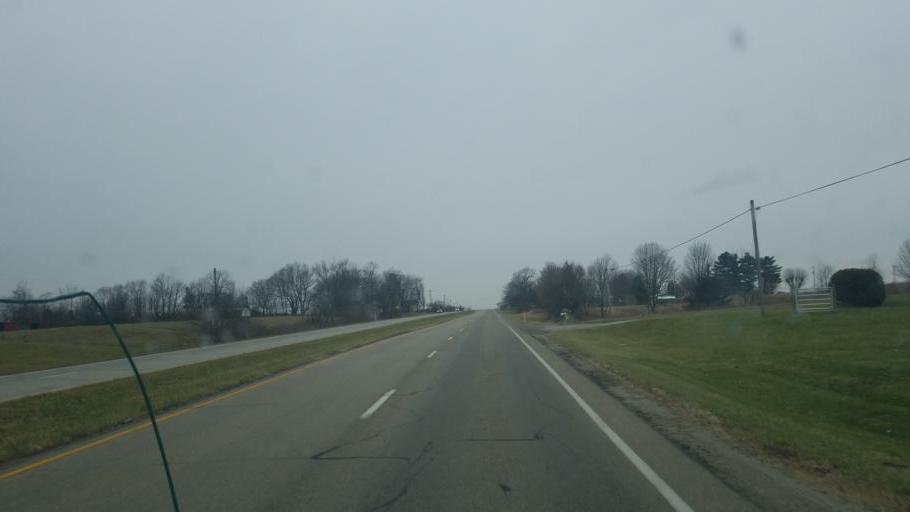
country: US
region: Indiana
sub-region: Henry County
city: Knightstown
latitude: 39.7939
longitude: -85.5475
